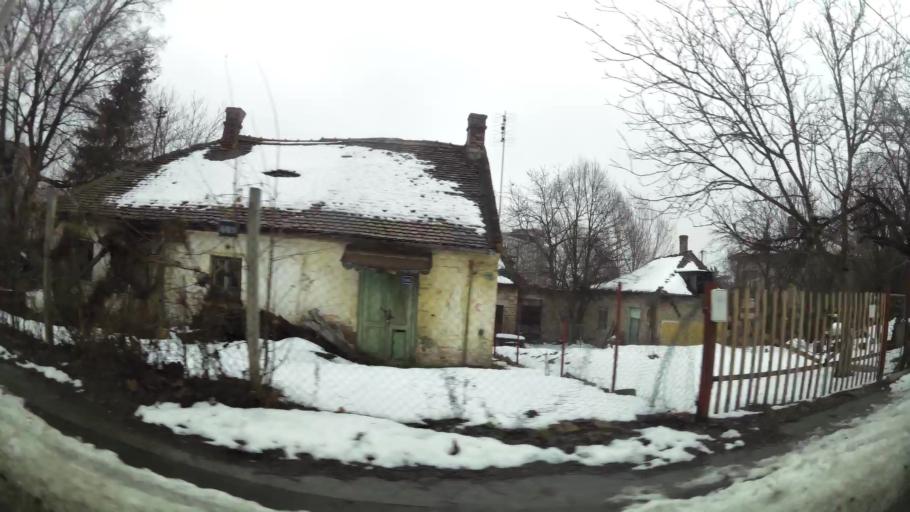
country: RS
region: Central Serbia
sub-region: Belgrade
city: Vozdovac
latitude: 44.7517
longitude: 20.4930
